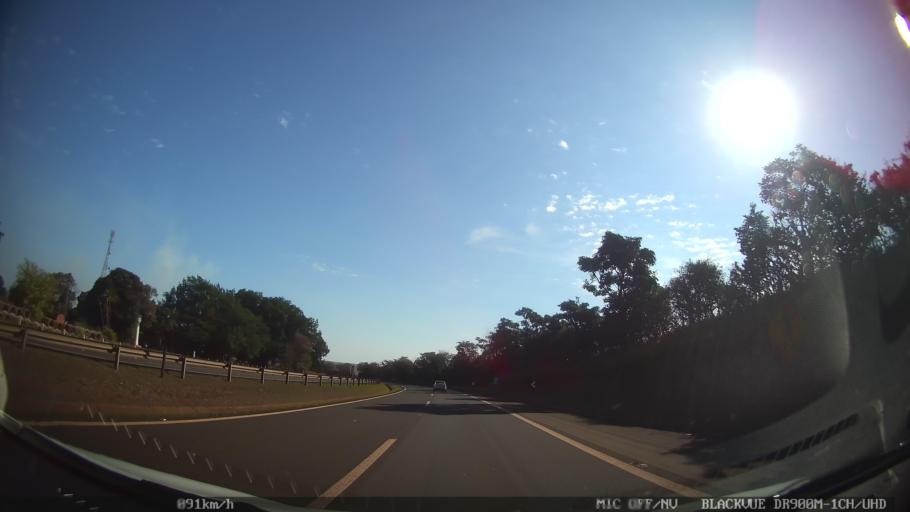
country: BR
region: Sao Paulo
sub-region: Iracemapolis
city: Iracemapolis
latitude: -22.6692
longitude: -47.5513
